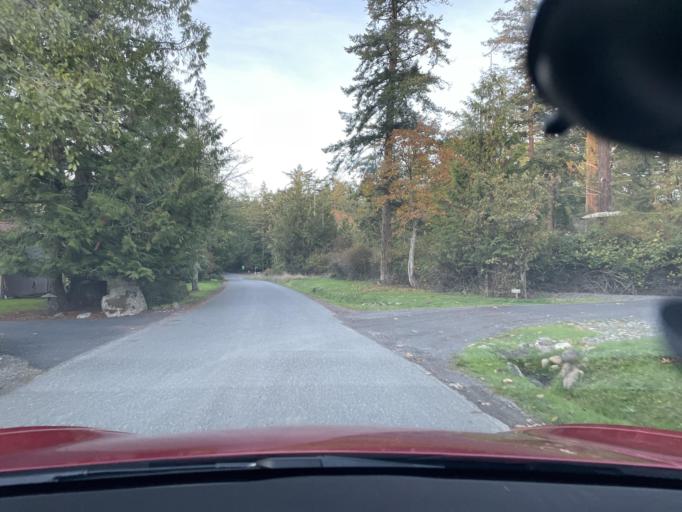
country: US
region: Washington
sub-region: San Juan County
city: Friday Harbor
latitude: 48.6186
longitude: -123.1501
